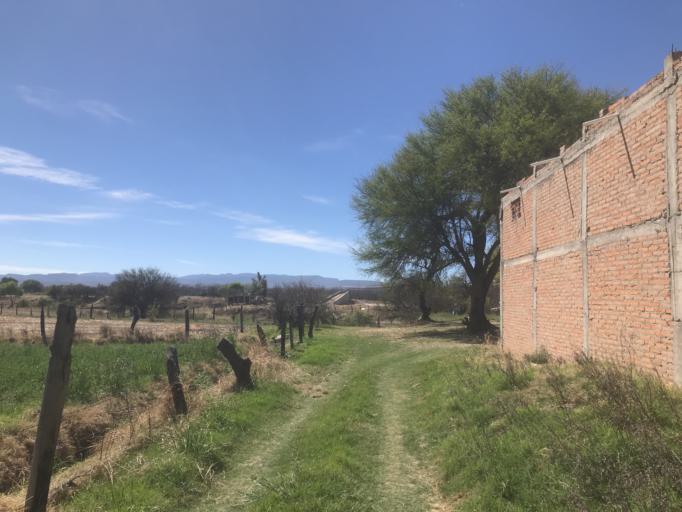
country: MX
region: Durango
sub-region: Durango
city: Sebastian Lerdo de Tejada
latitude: 23.9743
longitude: -104.6135
